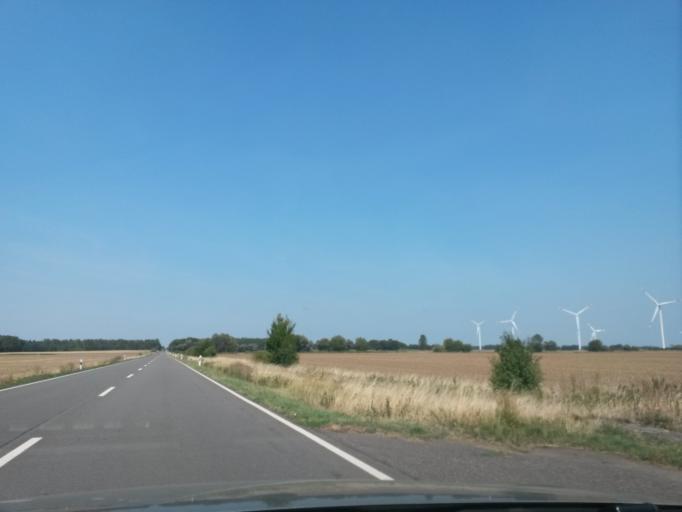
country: DE
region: Saxony-Anhalt
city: Jerichow
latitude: 52.5179
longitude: 12.0158
